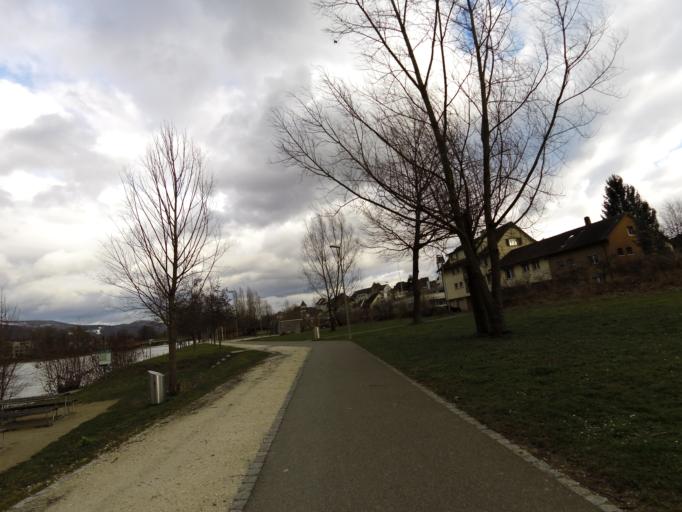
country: CH
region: Aargau
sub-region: Bezirk Aarau
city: Aarau
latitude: 47.3936
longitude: 8.0377
